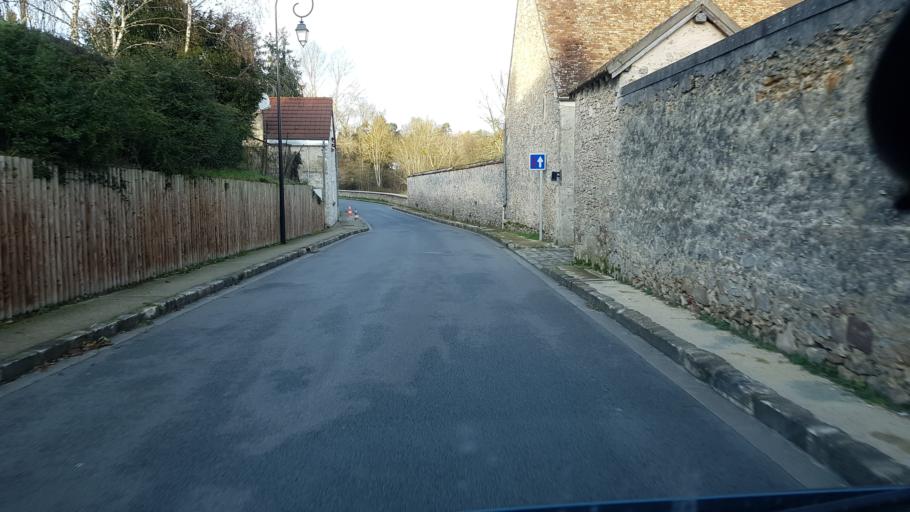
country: FR
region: Ile-de-France
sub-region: Departement des Yvelines
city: Saint-Leger-en-Yvelines
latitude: 48.6779
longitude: 1.7536
